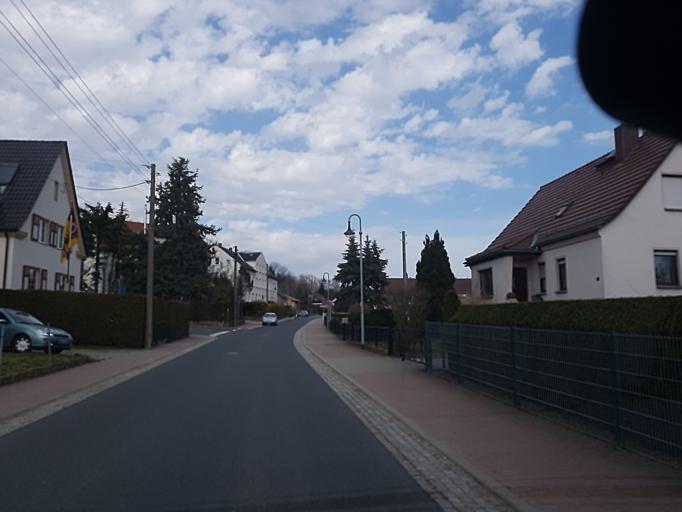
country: DE
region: Saxony
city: Grossweitzschen
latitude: 51.1390
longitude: 13.0313
